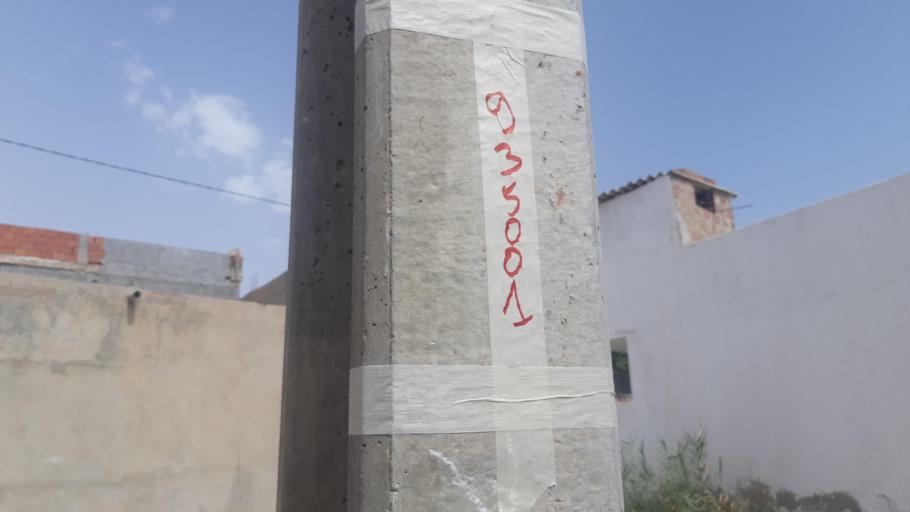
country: TN
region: Qabis
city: Gabes
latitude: 33.8958
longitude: 10.0928
